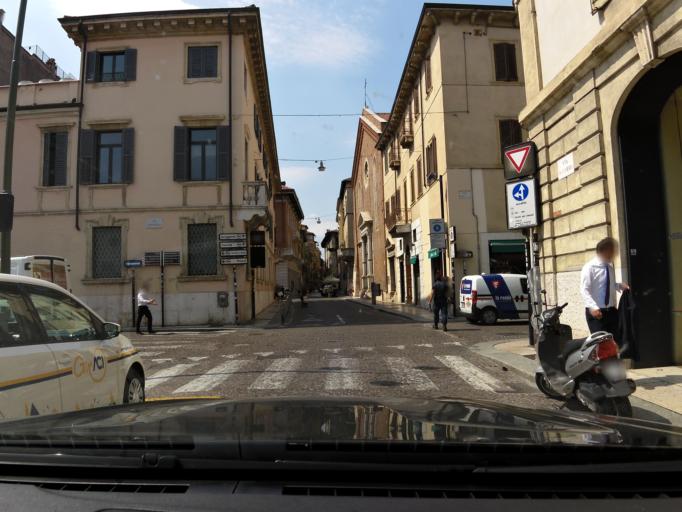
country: IT
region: Veneto
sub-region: Provincia di Verona
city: Verona
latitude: 45.4405
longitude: 10.9967
